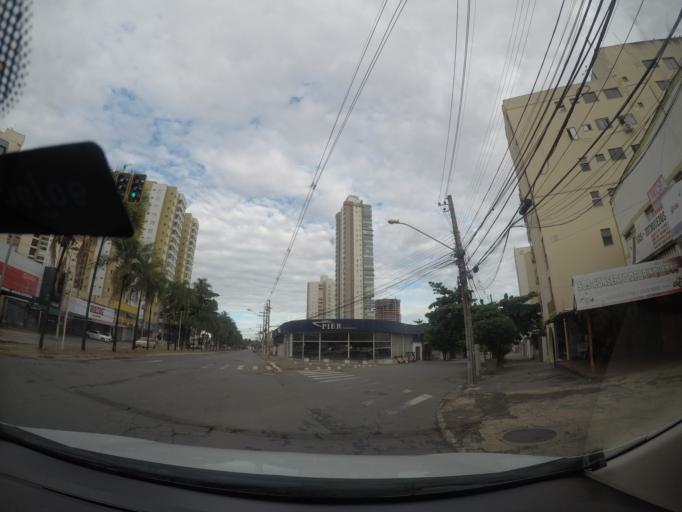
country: BR
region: Goias
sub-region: Goiania
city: Goiania
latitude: -16.6867
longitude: -49.2745
